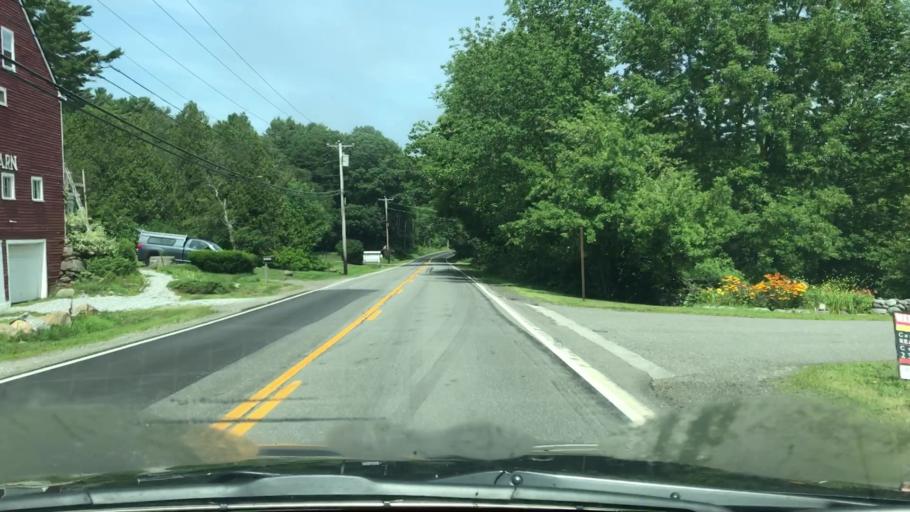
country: US
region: Maine
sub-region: Waldo County
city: Lincolnville
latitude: 44.2546
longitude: -69.0288
